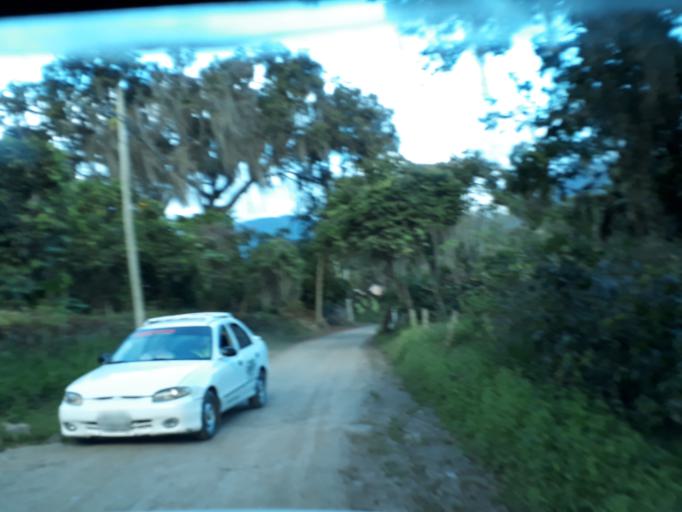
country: CO
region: Cundinamarca
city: Pacho
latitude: 5.1500
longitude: -74.1597
